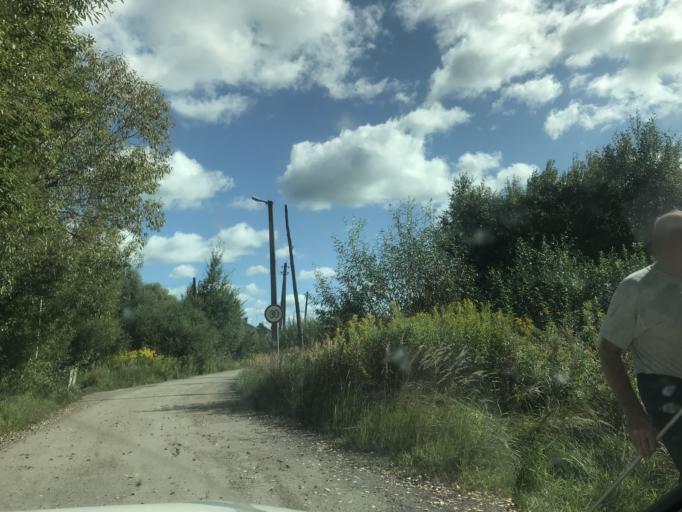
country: RU
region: Kaluga
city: Kondrovo
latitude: 54.7822
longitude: 35.9478
